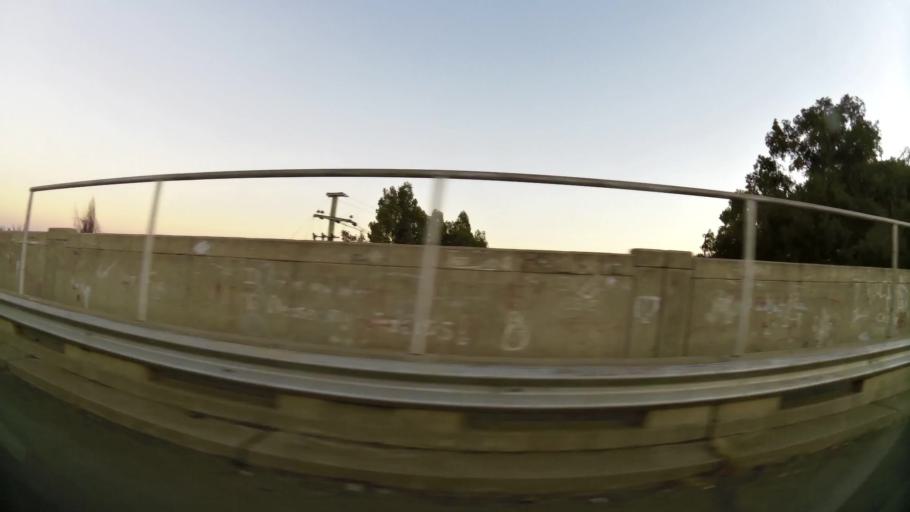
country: ZA
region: Northern Cape
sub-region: Frances Baard District Municipality
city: Kimberley
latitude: -28.7120
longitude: 24.7703
